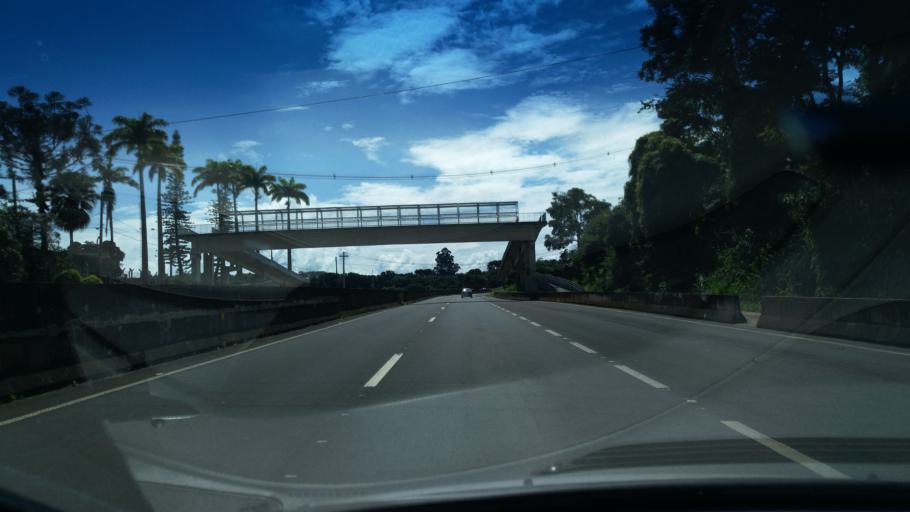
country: BR
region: Sao Paulo
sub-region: Santo Antonio Do Jardim
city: Espirito Santo do Pinhal
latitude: -22.1867
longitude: -46.7654
